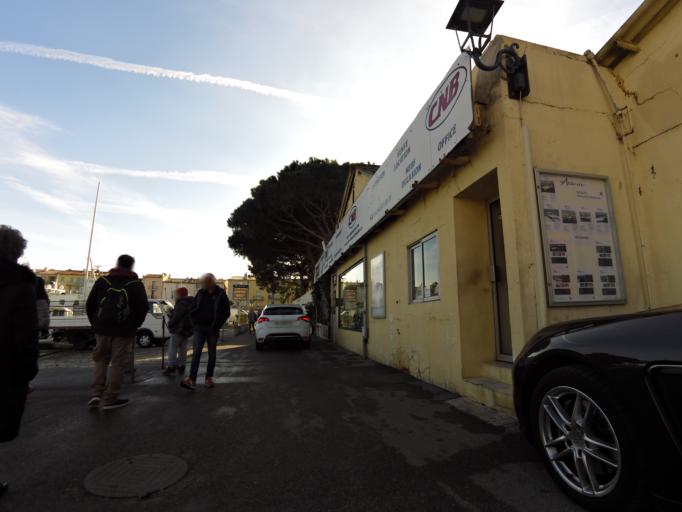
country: FR
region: Provence-Alpes-Cote d'Azur
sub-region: Departement du Var
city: Saint-Tropez
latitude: 43.2719
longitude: 6.6367
